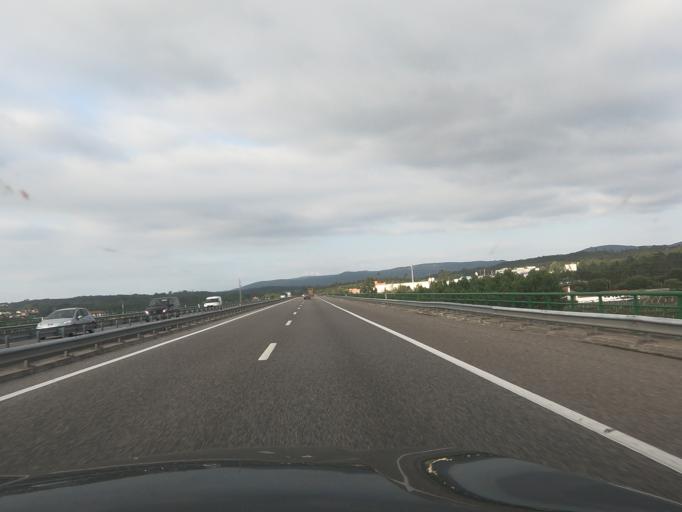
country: PT
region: Leiria
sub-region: Pombal
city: Pombal
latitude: 39.9740
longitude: -8.6392
